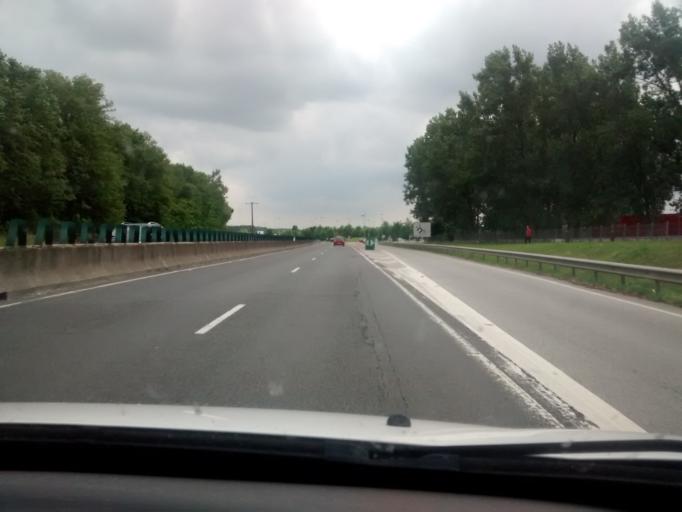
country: FR
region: Ile-de-France
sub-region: Departement des Yvelines
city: Rambouillet
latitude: 48.6298
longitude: 1.8319
